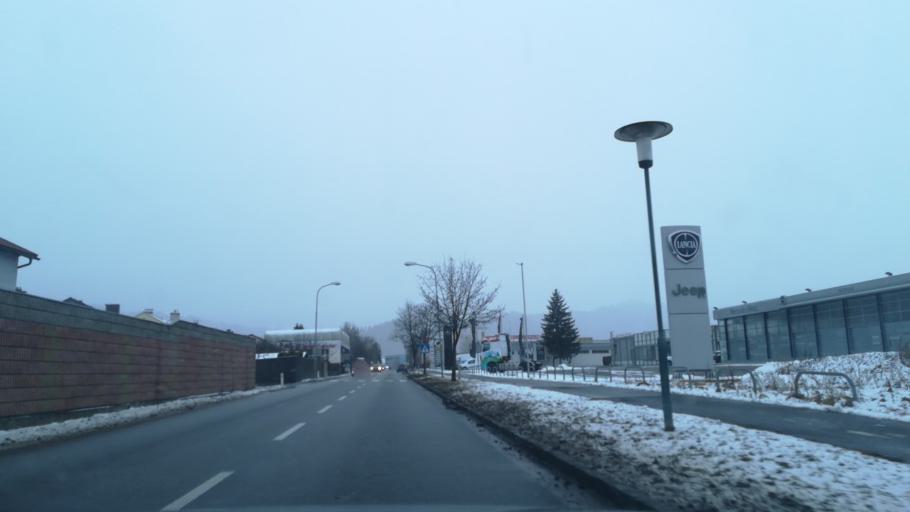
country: AT
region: Styria
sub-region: Politischer Bezirk Murtal
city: Fohnsdorf
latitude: 47.1829
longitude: 14.6783
